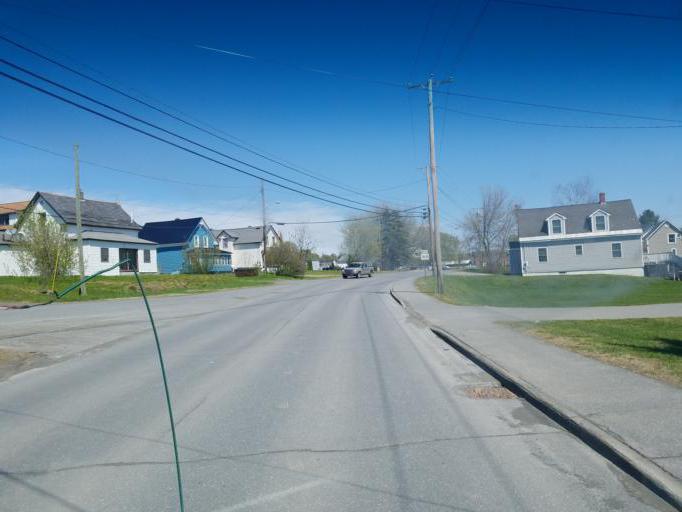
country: US
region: Maine
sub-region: Aroostook County
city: Caribou
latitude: 46.8582
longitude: -68.0202
